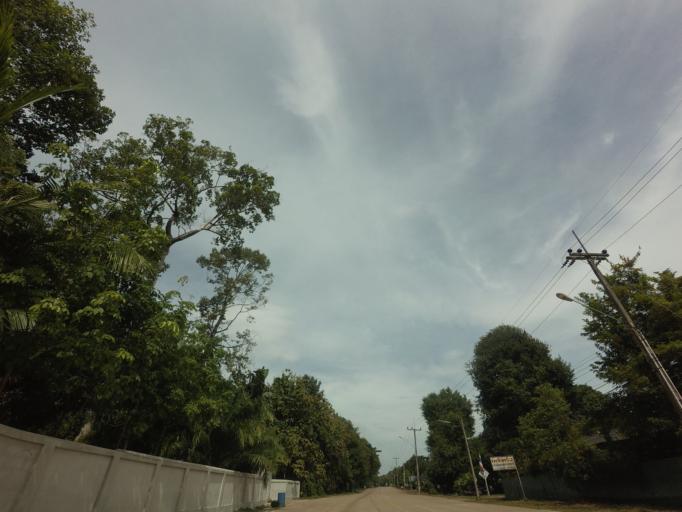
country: TH
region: Rayong
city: Klaeng
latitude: 12.6503
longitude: 101.5644
